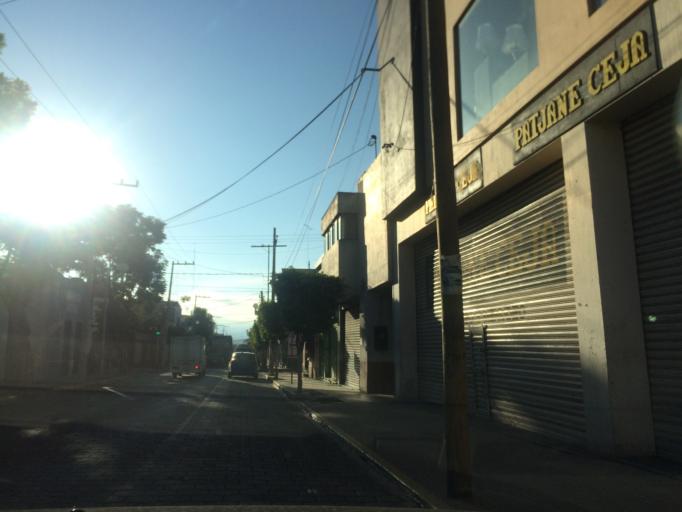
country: MX
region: Puebla
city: Tehuacan
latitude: 18.4633
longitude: -97.4007
